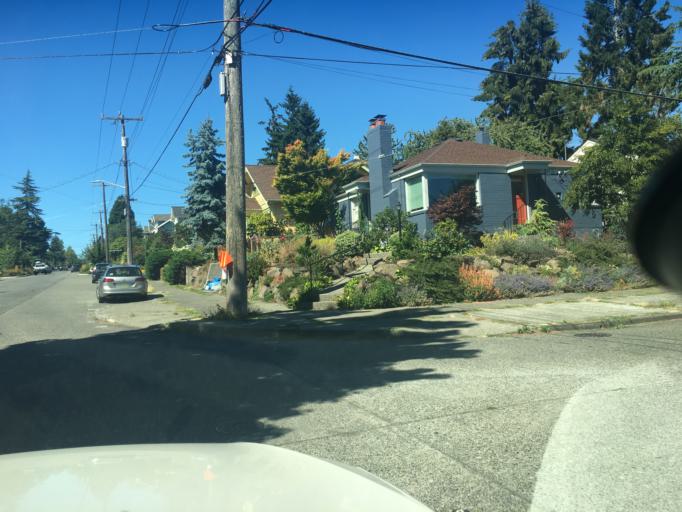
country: US
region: Washington
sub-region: King County
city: Shoreline
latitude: 47.6794
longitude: -122.3929
